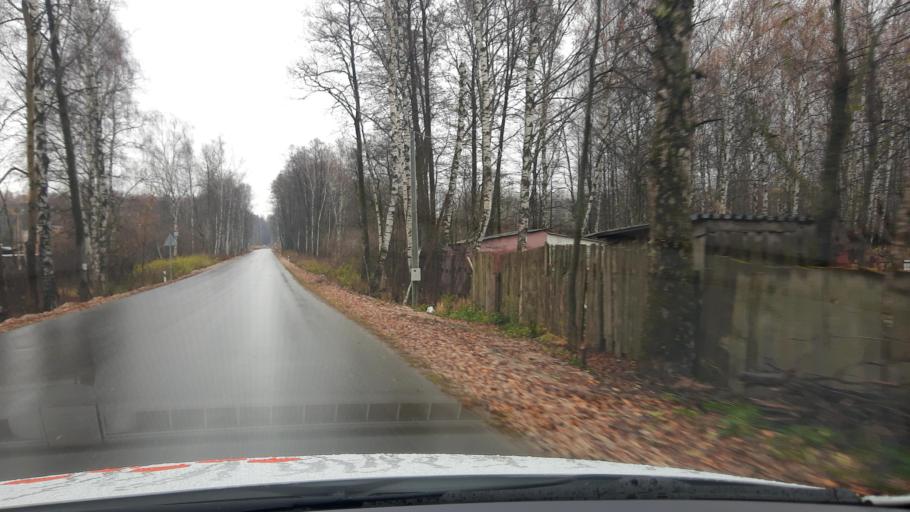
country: RU
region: Moskovskaya
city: Elektrostal'
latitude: 55.7951
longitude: 38.3702
